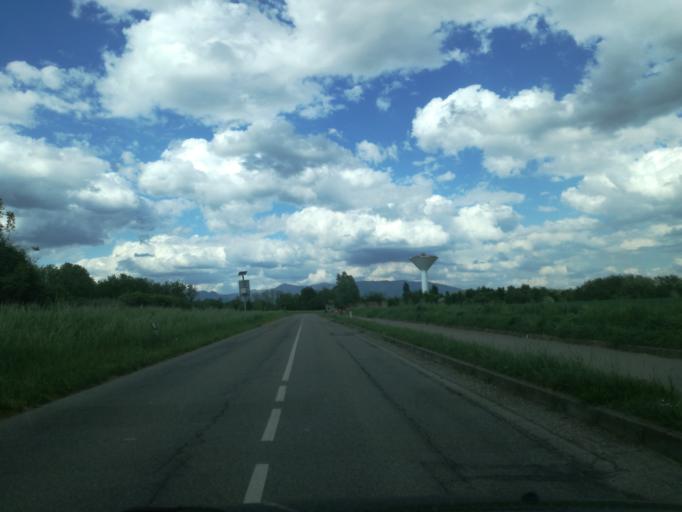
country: IT
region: Lombardy
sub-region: Provincia di Monza e Brianza
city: Carnate
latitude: 45.6548
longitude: 9.3841
